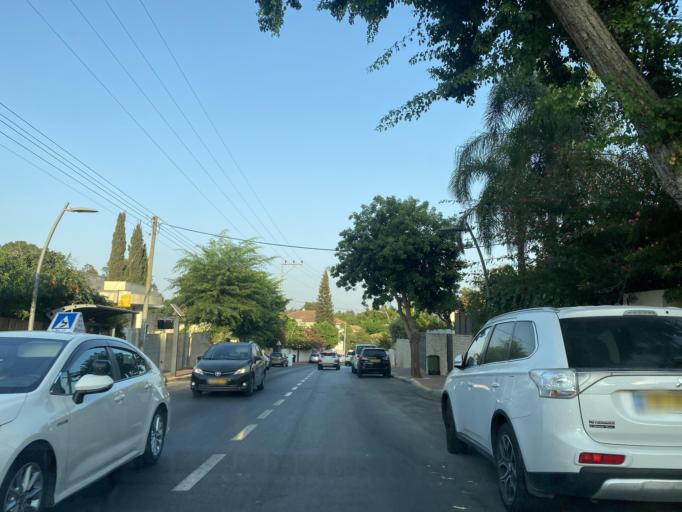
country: IL
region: Tel Aviv
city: Ramat HaSharon
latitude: 32.1359
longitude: 34.8546
